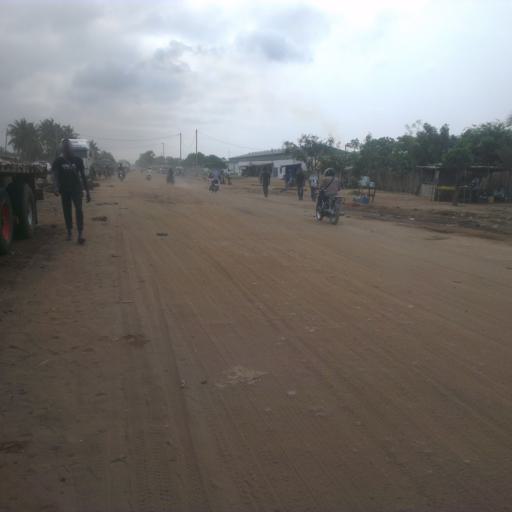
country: TG
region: Maritime
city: Lome
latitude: 6.1600
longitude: 1.2895
